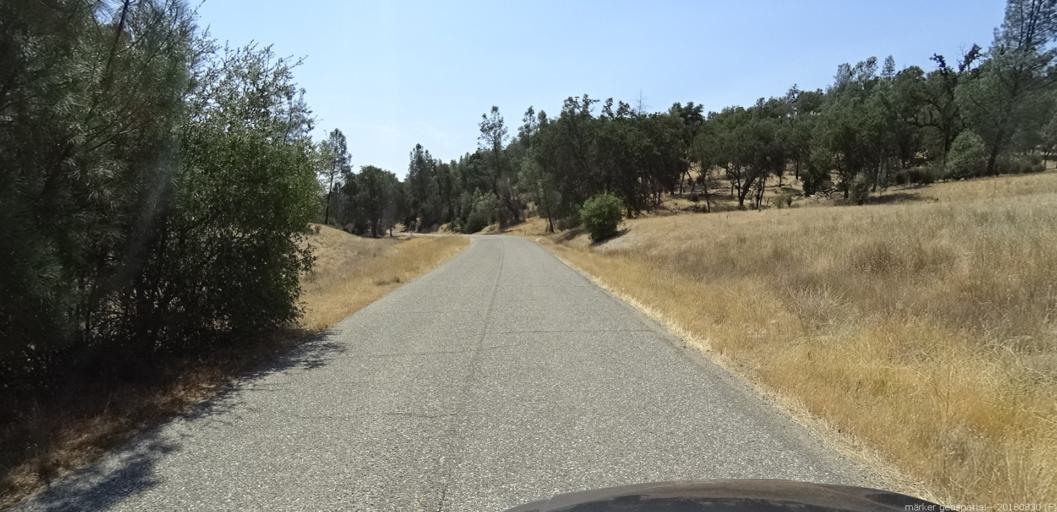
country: US
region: California
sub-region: Monterey County
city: King City
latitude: 35.9908
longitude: -121.2623
